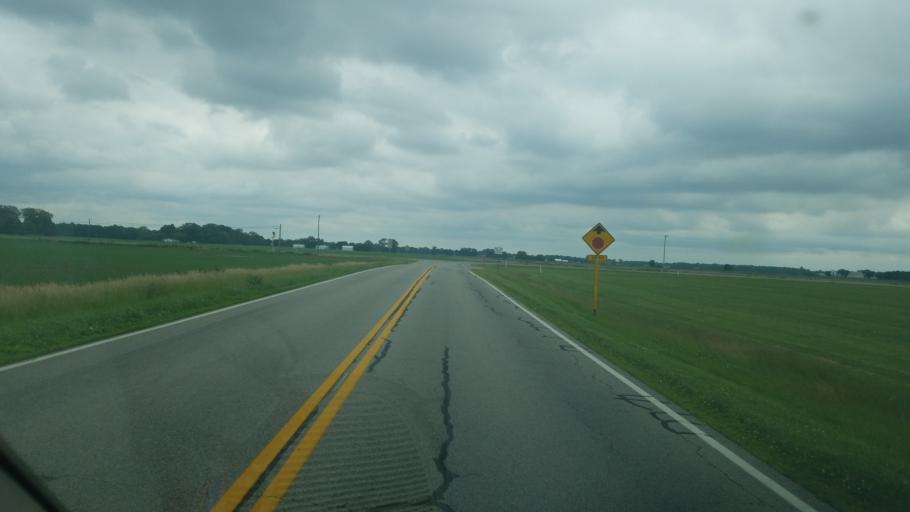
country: US
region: Ohio
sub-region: Marion County
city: Marion
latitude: 40.5845
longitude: -83.0101
